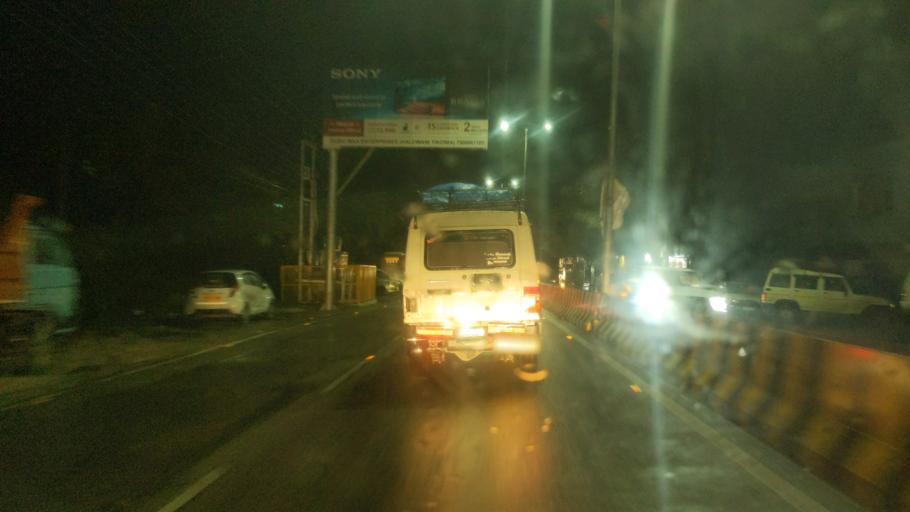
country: IN
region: Uttarakhand
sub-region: Naini Tal
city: Haldwani
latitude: 29.2614
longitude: 79.5438
